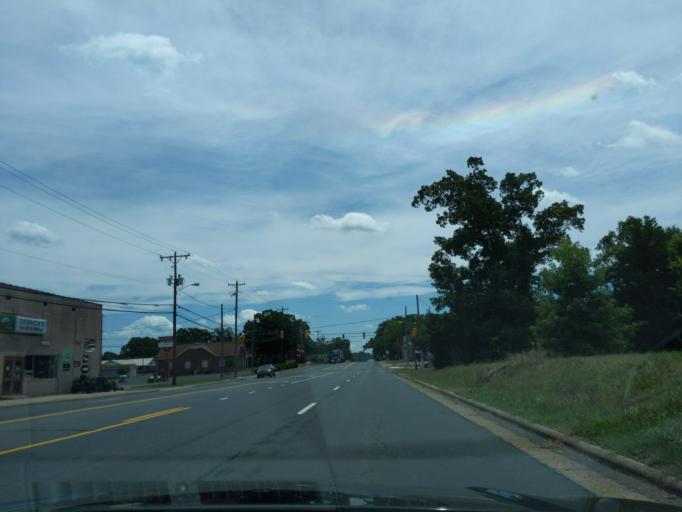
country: US
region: North Carolina
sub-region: Stanly County
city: Albemarle
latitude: 35.4683
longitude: -80.2607
